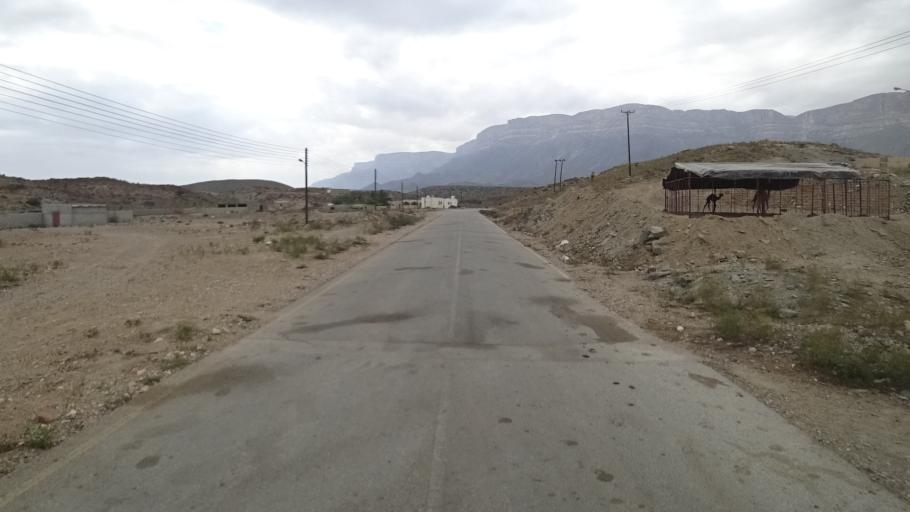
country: OM
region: Zufar
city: Salalah
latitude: 17.1661
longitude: 54.9798
